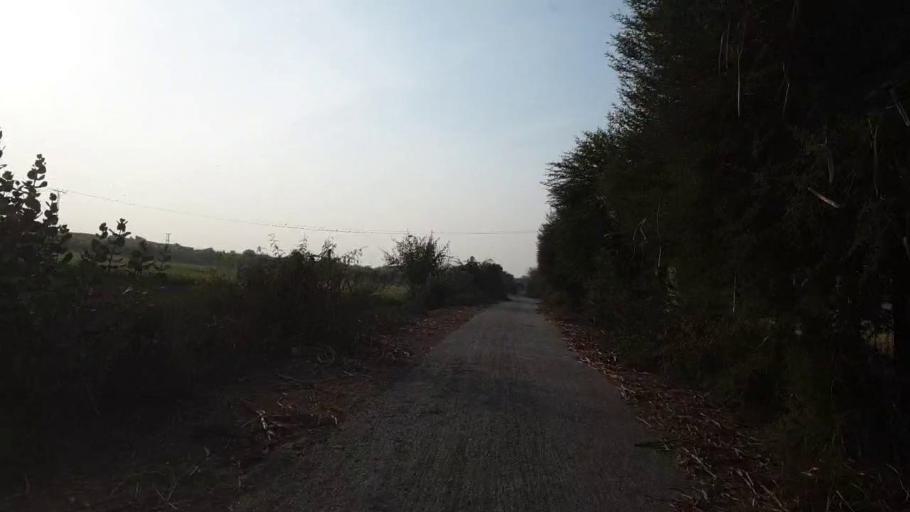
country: PK
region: Sindh
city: Matiari
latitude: 25.5995
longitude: 68.4362
